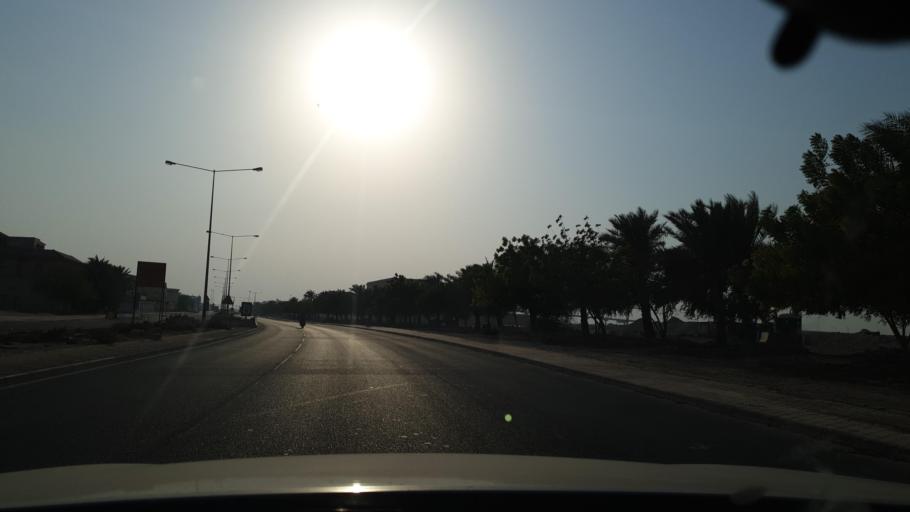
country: QA
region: Al Wakrah
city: Al Wakrah
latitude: 25.1960
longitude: 51.6053
